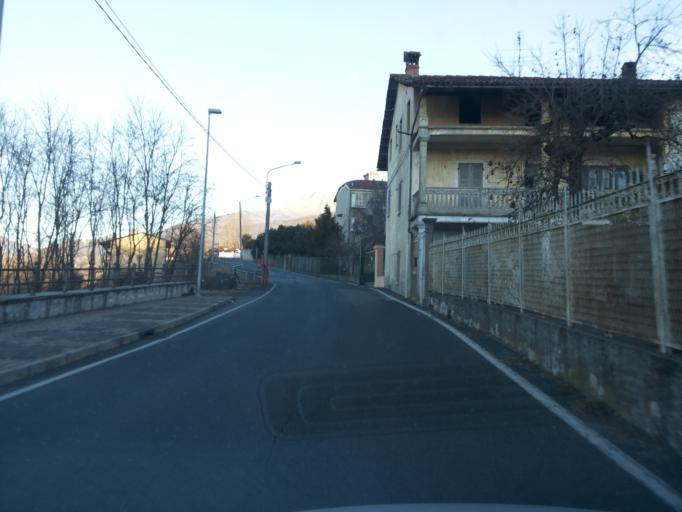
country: IT
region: Piedmont
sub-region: Provincia di Torino
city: Burolo
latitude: 45.4790
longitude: 7.9349
